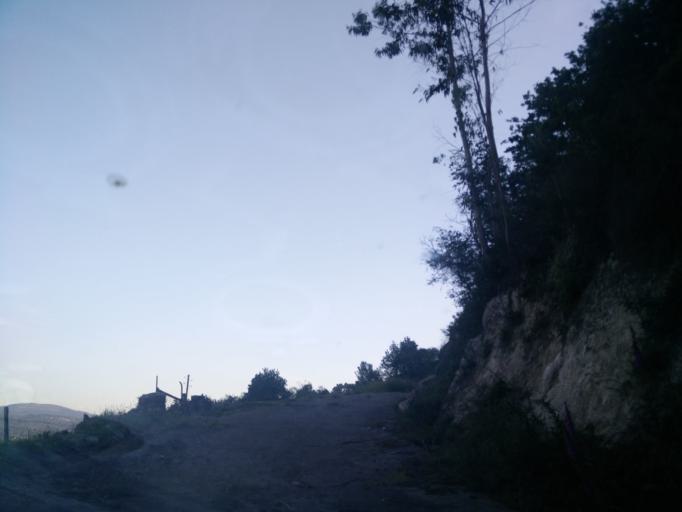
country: ES
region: Galicia
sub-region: Provincia de Pontevedra
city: Mondariz
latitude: 42.2685
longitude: -8.4085
